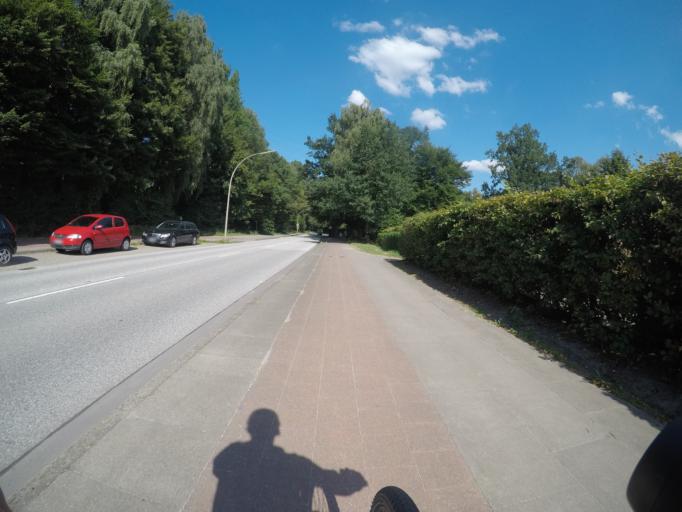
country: DE
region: Hamburg
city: Bergedorf
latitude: 53.5133
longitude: 10.2131
